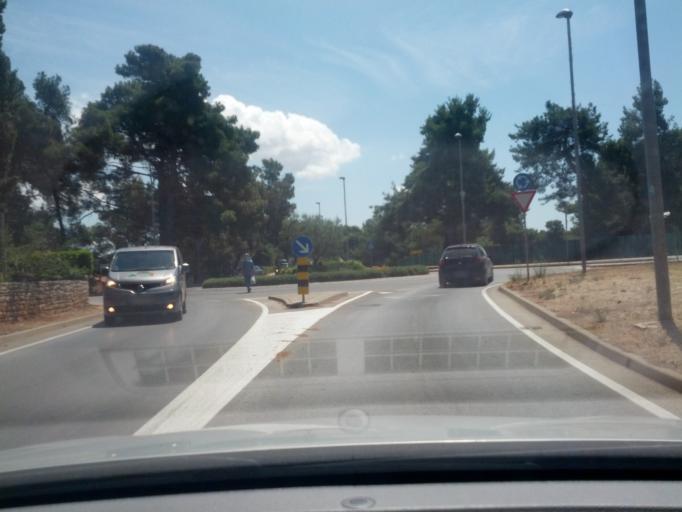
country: HR
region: Istarska
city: Fazana
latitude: 44.9161
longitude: 13.8146
